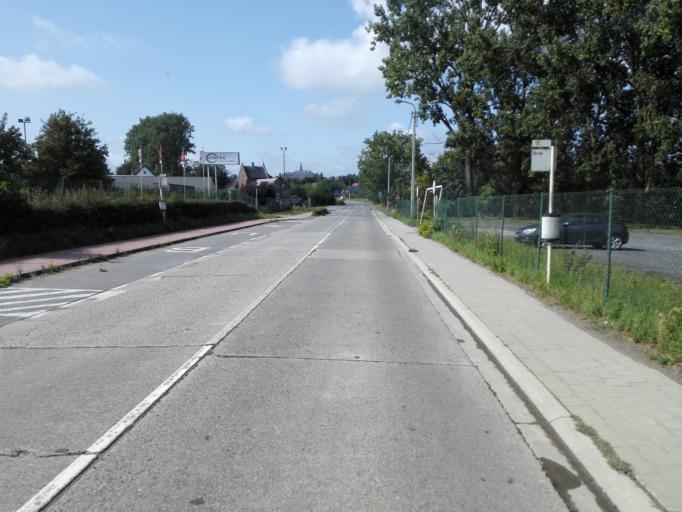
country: BE
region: Flanders
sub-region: Provincie Vlaams-Brabant
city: Asse
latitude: 50.9161
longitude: 4.2152
